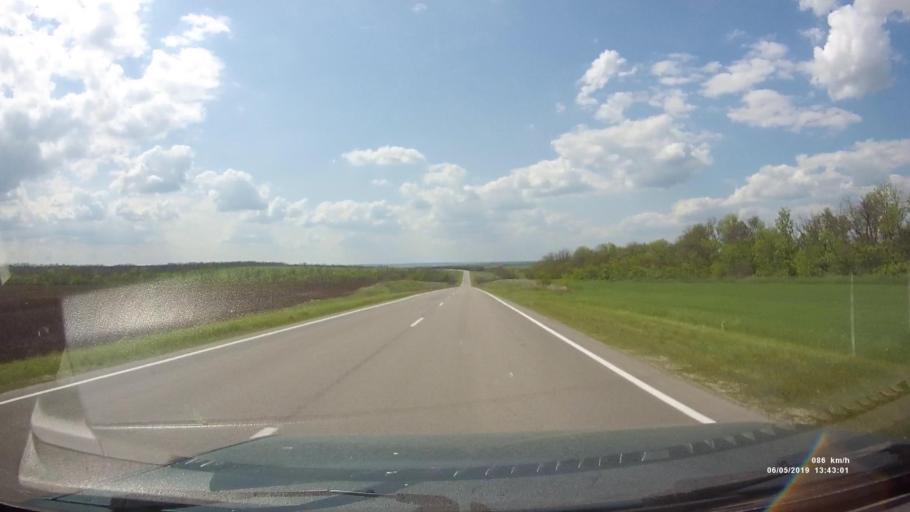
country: RU
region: Rostov
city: Semikarakorsk
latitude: 47.6599
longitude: 40.6464
